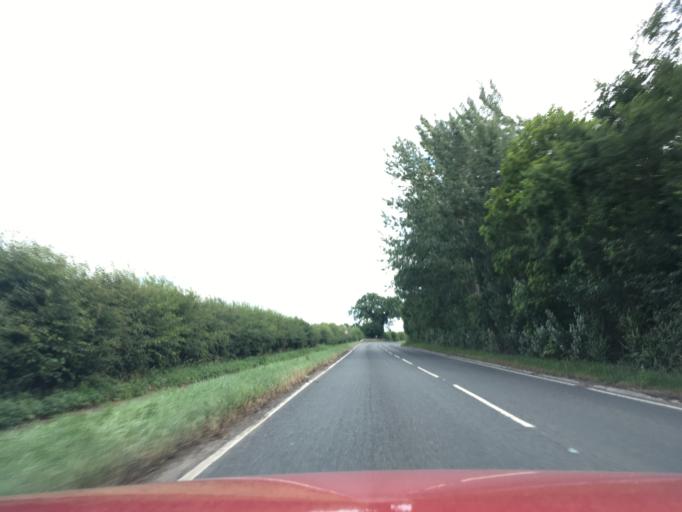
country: GB
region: England
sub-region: Warwickshire
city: Nuneaton
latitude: 52.5524
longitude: -1.4786
